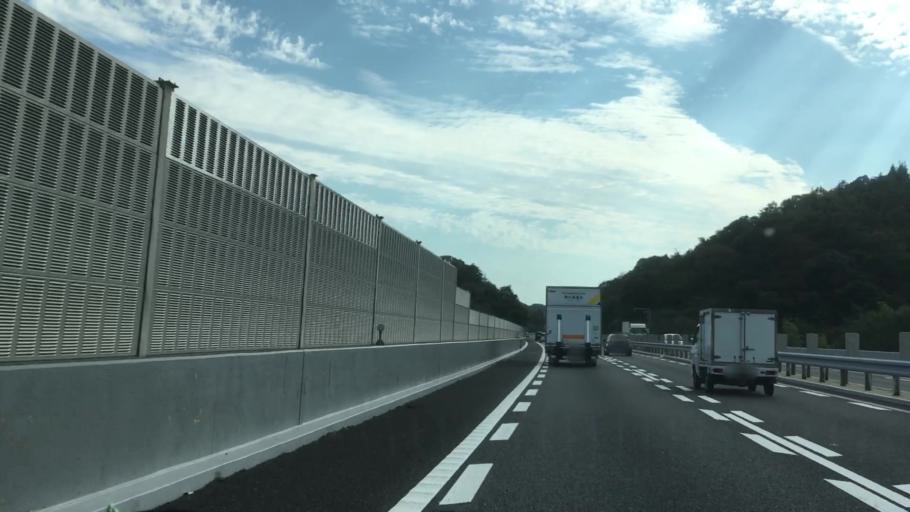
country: JP
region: Hiroshima
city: Ono-hara
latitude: 34.3133
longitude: 132.2807
